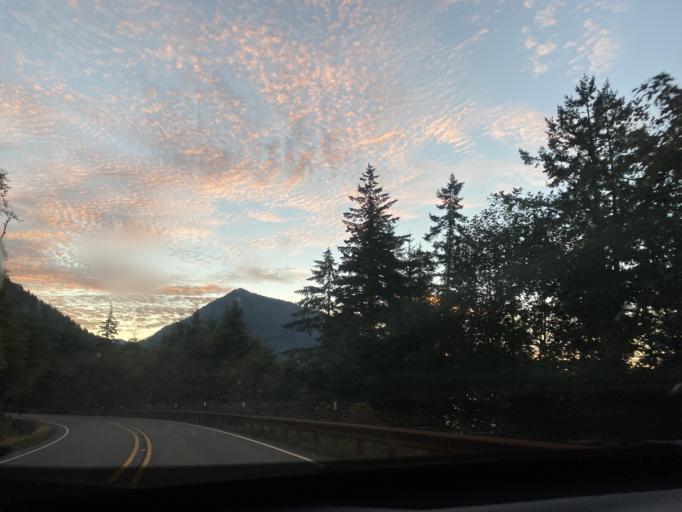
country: CA
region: British Columbia
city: Sooke
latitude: 48.0793
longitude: -123.7512
